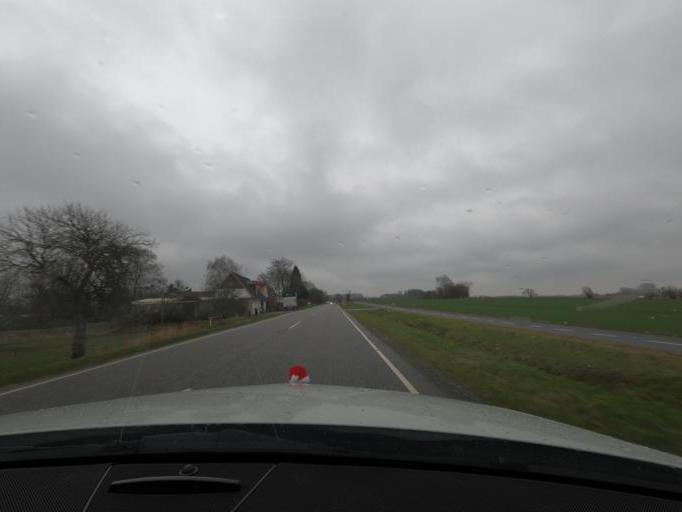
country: DK
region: South Denmark
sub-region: Haderslev Kommune
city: Starup
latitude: 55.2542
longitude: 9.6280
